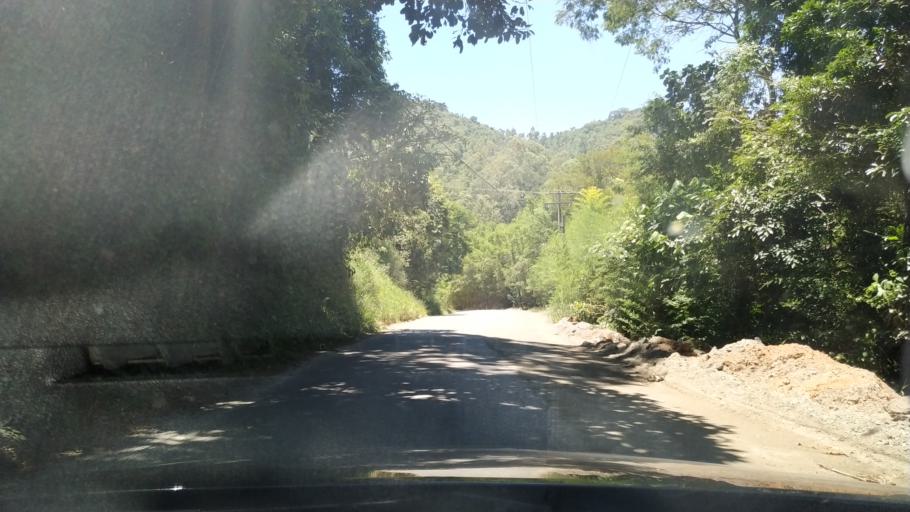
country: BR
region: Sao Paulo
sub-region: Campos Do Jordao
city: Campos do Jordao
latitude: -22.8058
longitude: -45.6901
